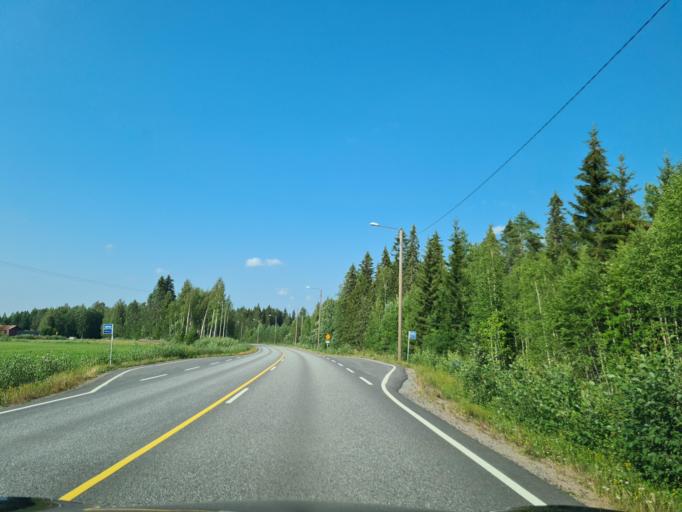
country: FI
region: Satakunta
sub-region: Pohjois-Satakunta
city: Karvia
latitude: 62.0830
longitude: 22.5247
